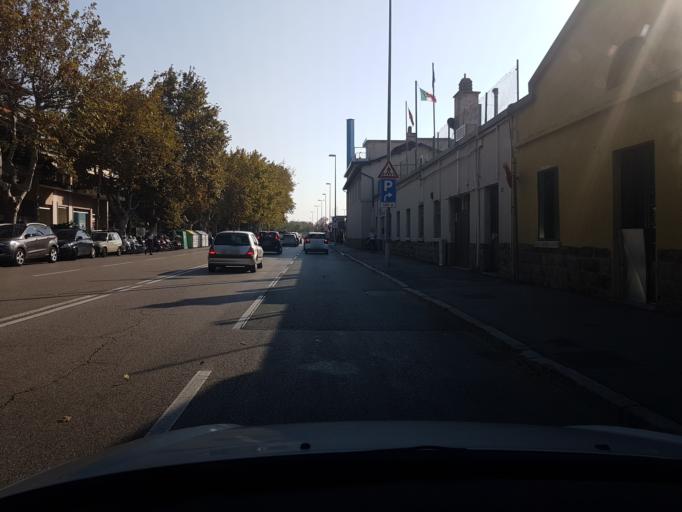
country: IT
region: Friuli Venezia Giulia
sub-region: Provincia di Trieste
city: Villa Opicina
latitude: 45.6791
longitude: 13.7546
